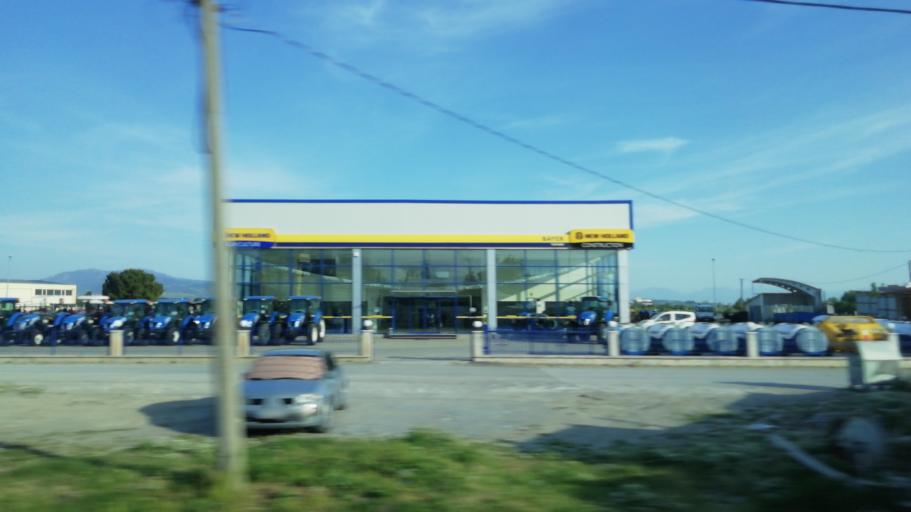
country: TR
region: Manisa
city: Saruhanli
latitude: 38.7276
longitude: 27.5759
